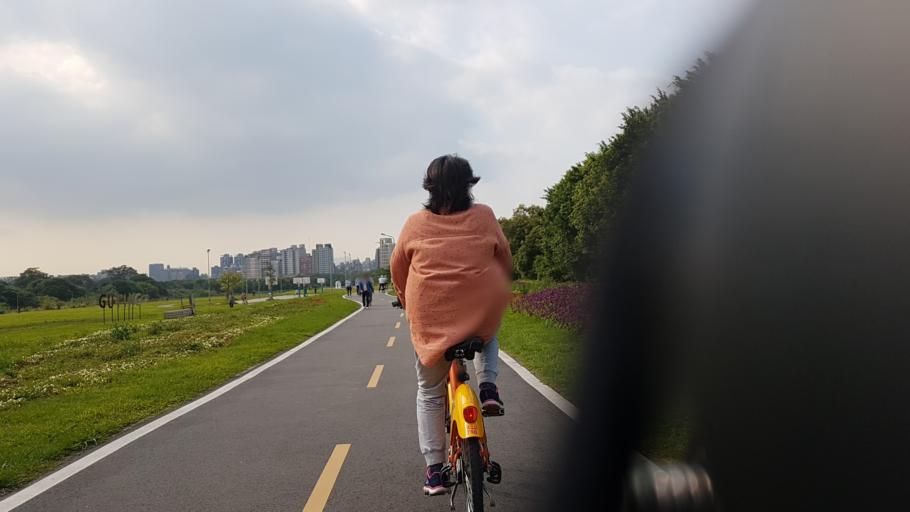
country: TW
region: Taipei
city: Taipei
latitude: 25.0134
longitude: 121.5267
